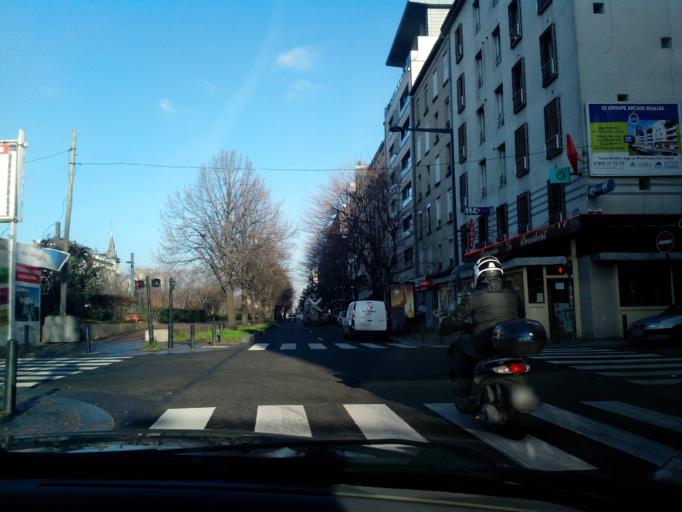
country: FR
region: Ile-de-France
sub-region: Paris
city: Saint-Ouen
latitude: 48.9064
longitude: 2.3588
